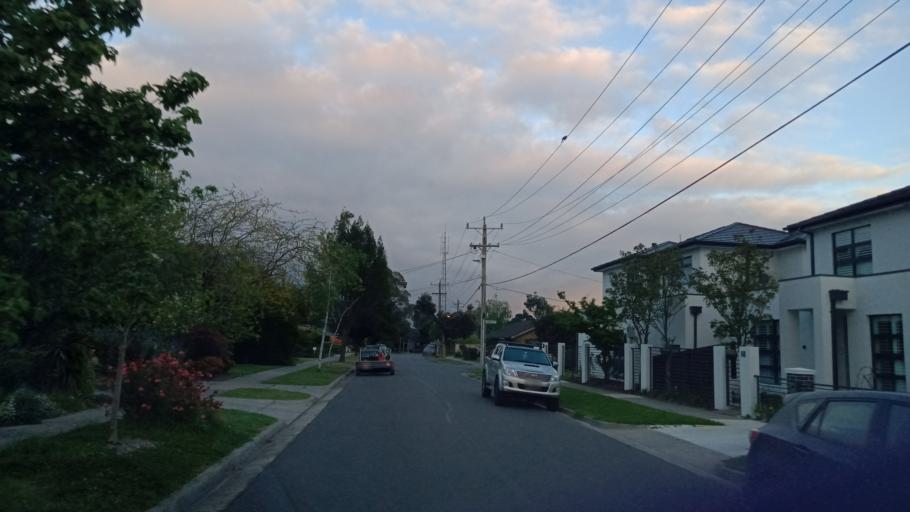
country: AU
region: Victoria
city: Burwood East
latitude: -37.8748
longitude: 145.1402
